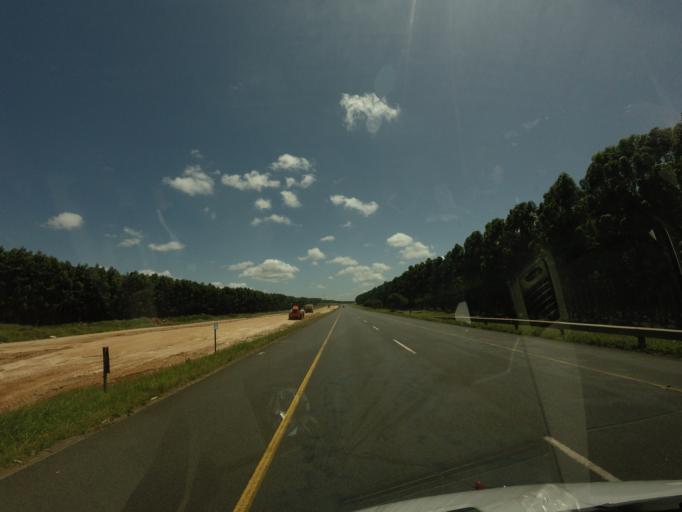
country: ZA
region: KwaZulu-Natal
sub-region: uThungulu District Municipality
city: Empangeni
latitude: -28.7452
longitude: 31.9376
